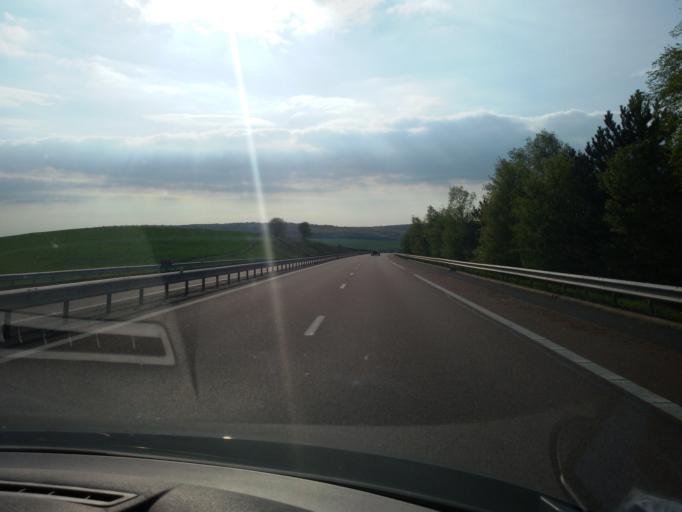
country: FR
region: Champagne-Ardenne
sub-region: Departement de l'Aube
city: Bar-sur-Aube
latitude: 48.1294
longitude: 4.6724
